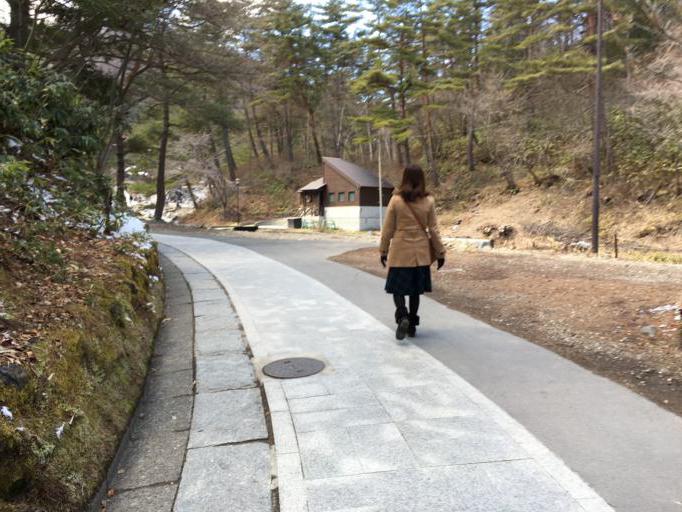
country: JP
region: Gunma
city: Nakanojomachi
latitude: 36.6242
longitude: 138.5909
